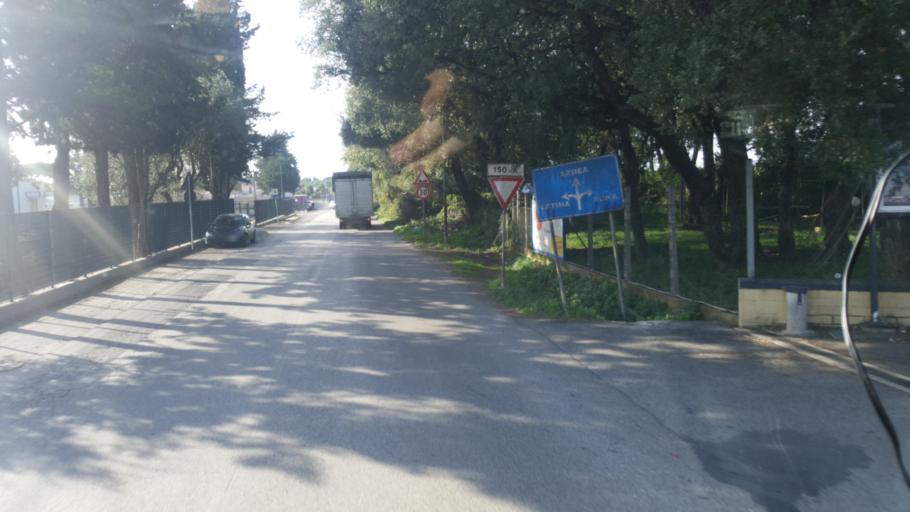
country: IT
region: Latium
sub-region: Provincia di Latina
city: Casalazzara
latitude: 41.6247
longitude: 12.5859
